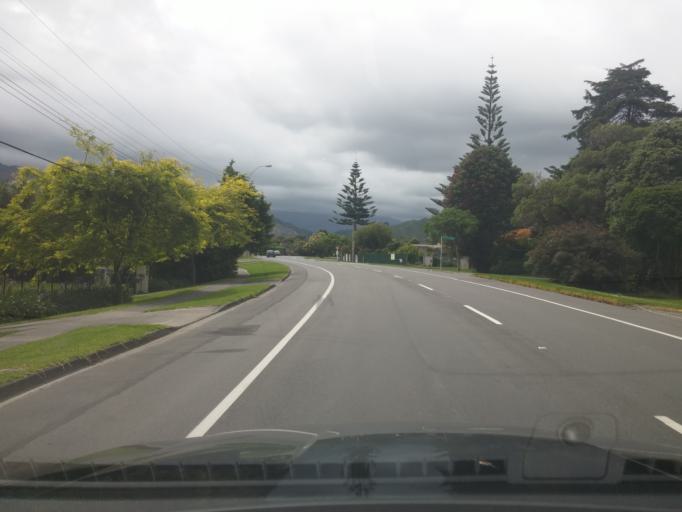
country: NZ
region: Wellington
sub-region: Kapiti Coast District
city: Paraparaumu
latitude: -40.8736
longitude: 175.0389
